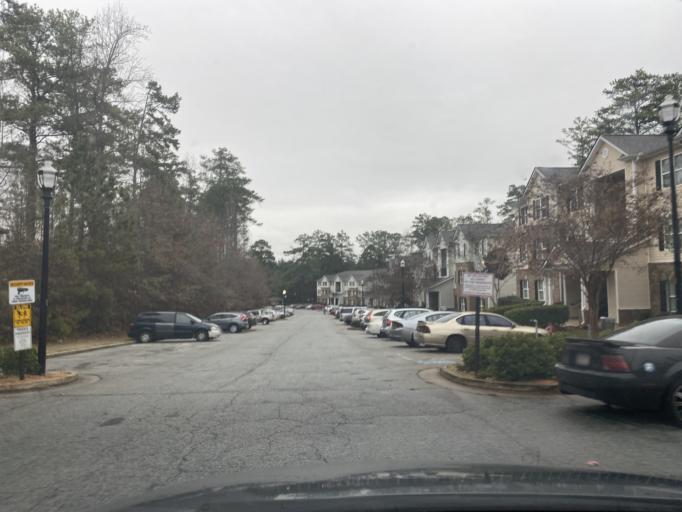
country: US
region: Georgia
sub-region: DeKalb County
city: Pine Mountain
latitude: 33.6985
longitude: -84.1542
